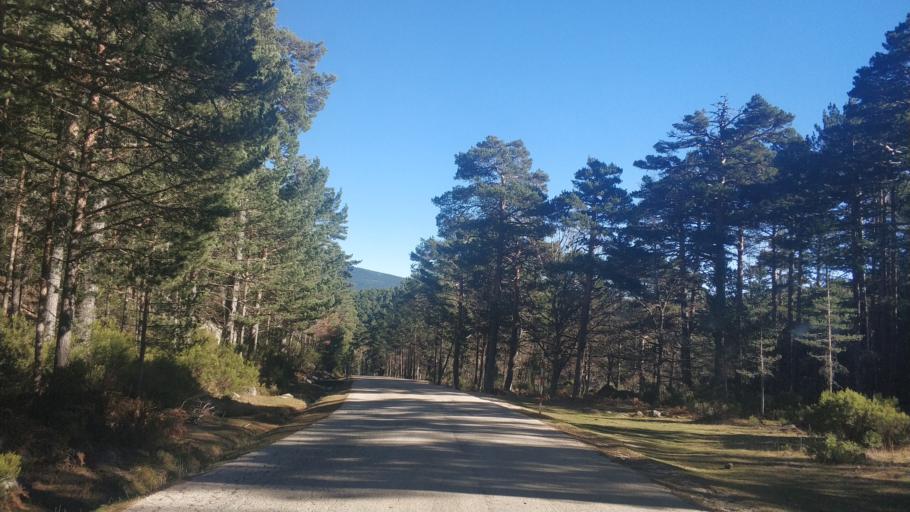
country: ES
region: Castille and Leon
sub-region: Provincia de Soria
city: Covaleda
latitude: 41.9969
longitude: -2.8318
